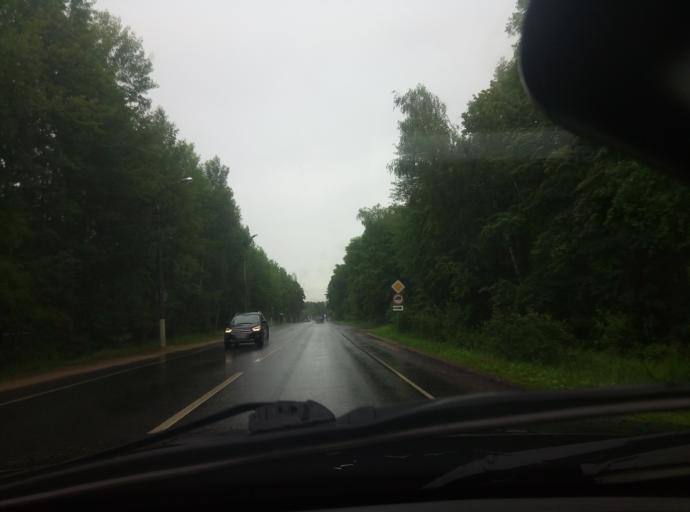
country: RU
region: Moskovskaya
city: Protvino
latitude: 54.8809
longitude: 37.2319
